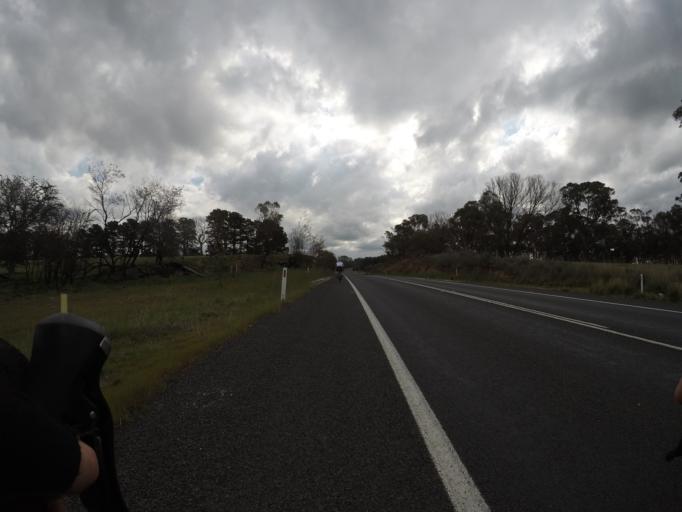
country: AU
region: New South Wales
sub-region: Blayney
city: Blayney
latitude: -33.4313
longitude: 149.3239
